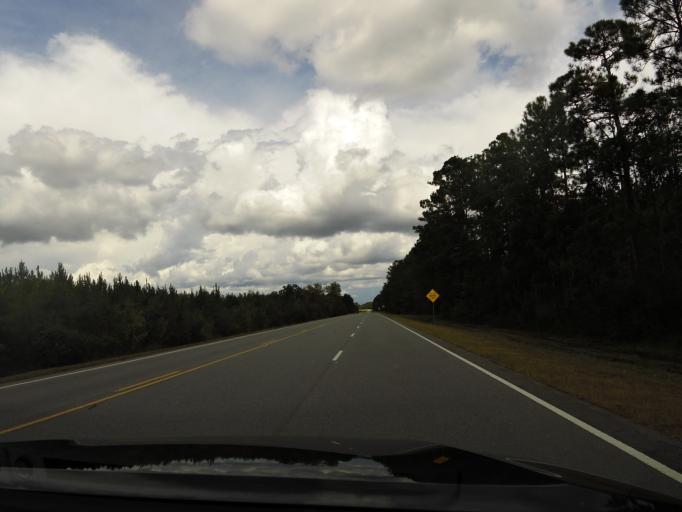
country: US
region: Georgia
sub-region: Brantley County
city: Nahunta
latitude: 31.0894
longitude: -82.0079
